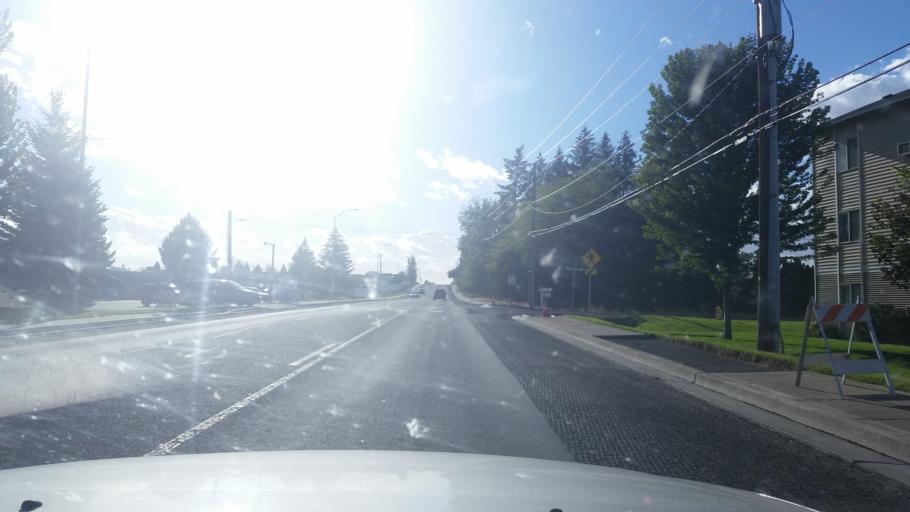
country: US
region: Washington
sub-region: Spokane County
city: Cheney
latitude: 47.5073
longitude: -117.5695
